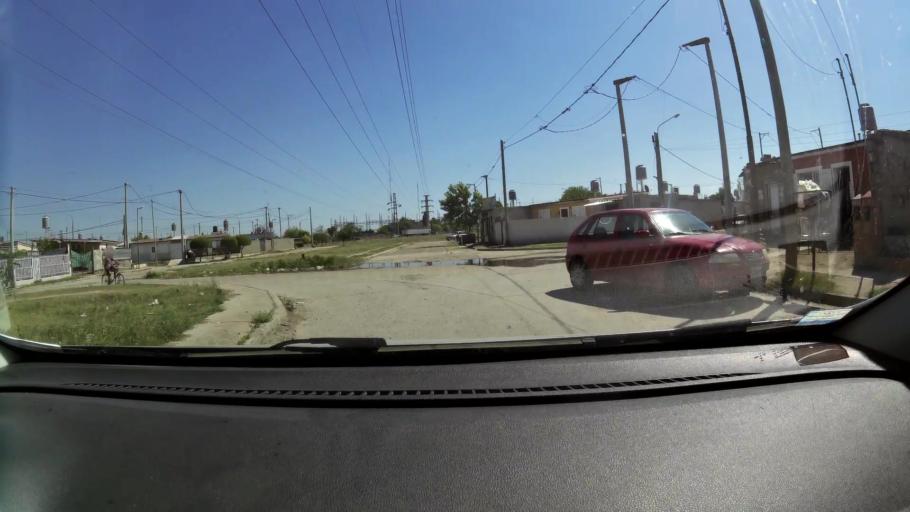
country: AR
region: Cordoba
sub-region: Departamento de Capital
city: Cordoba
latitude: -31.3709
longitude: -64.1636
